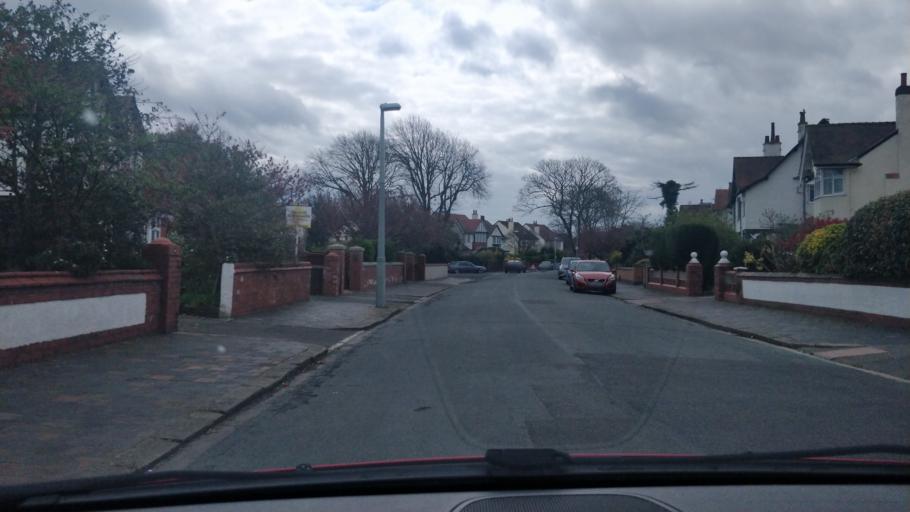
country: GB
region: England
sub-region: Sefton
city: Formby
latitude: 53.6052
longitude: -3.0443
